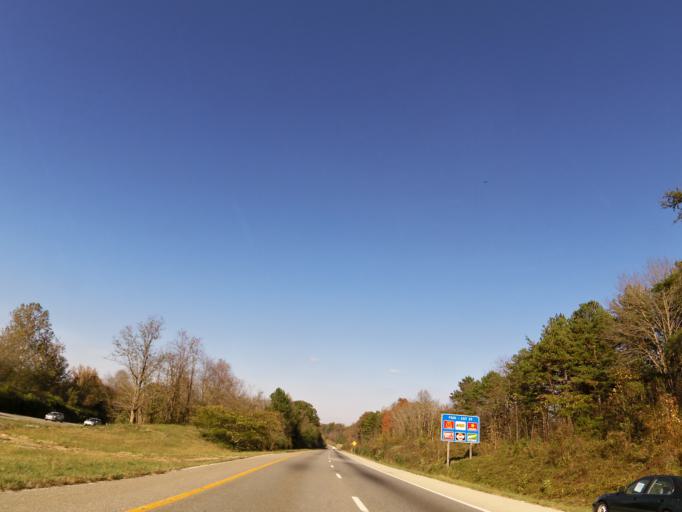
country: US
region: Kentucky
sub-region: Whitley County
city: Corbin
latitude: 36.9594
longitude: -84.1172
